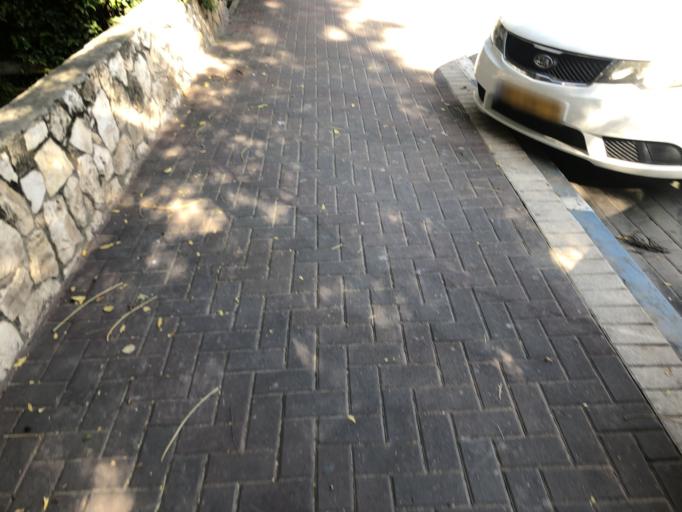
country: IL
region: Tel Aviv
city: Giv`atayim
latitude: 32.0723
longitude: 34.8123
